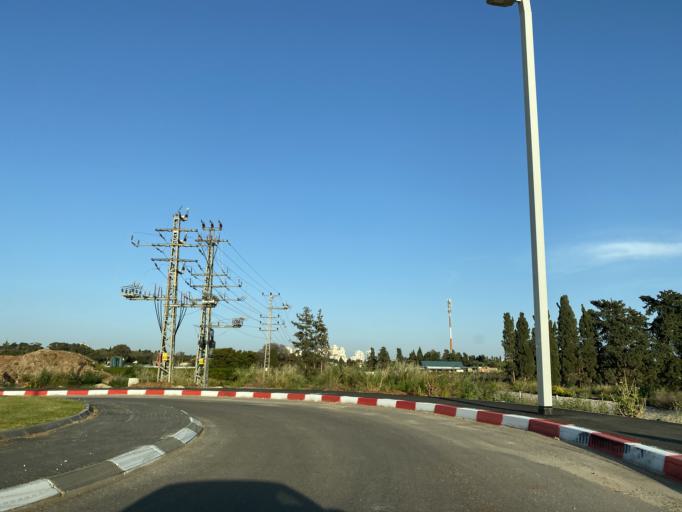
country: IL
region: Tel Aviv
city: Herzliyya
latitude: 32.1558
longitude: 34.8219
